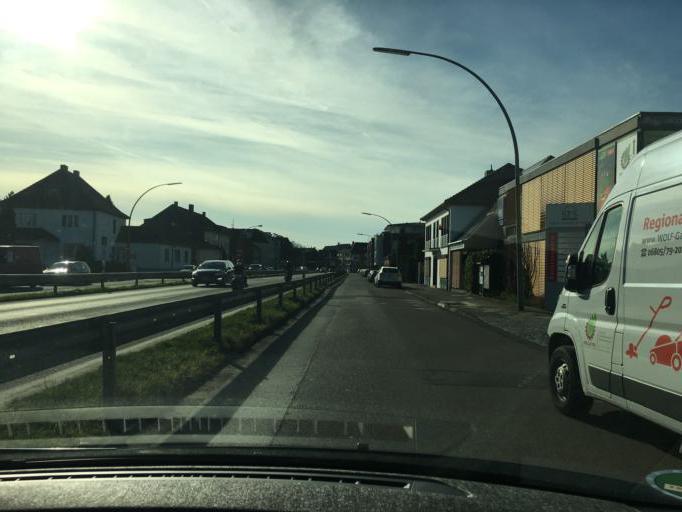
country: DE
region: North Rhine-Westphalia
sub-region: Regierungsbezirk Dusseldorf
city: Korschenbroich
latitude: 51.1944
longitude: 6.5164
